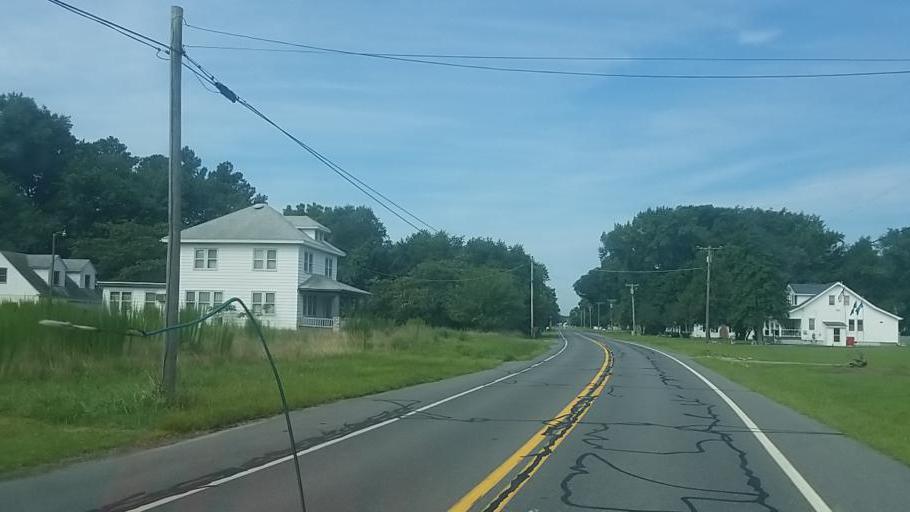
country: US
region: Delaware
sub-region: Sussex County
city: Selbyville
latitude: 38.5273
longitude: -75.2076
